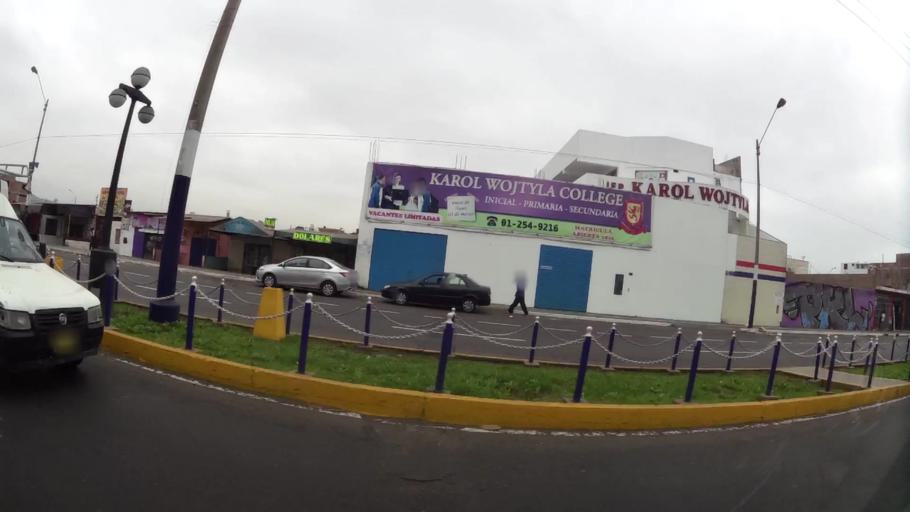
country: PE
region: Lima
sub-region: Lima
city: Surco
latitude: -12.1974
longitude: -77.0115
